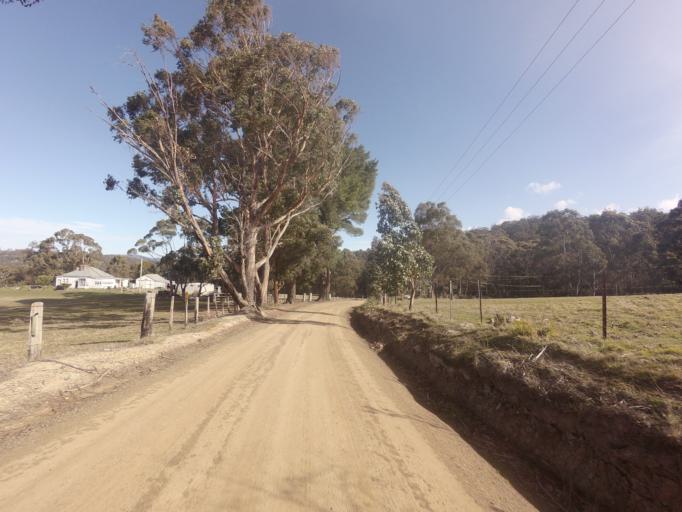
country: AU
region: Tasmania
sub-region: Kingborough
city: Kettering
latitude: -43.1011
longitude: 147.2634
